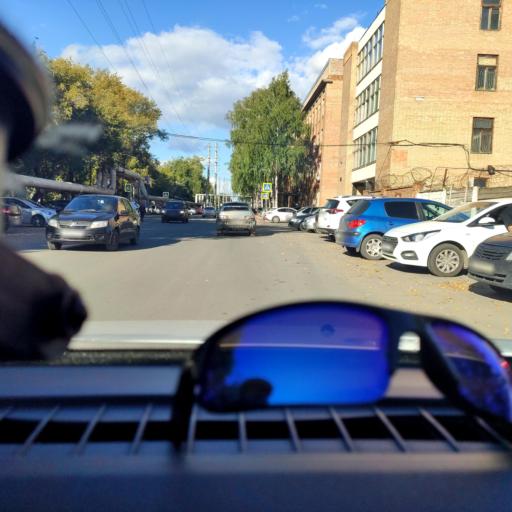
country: RU
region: Samara
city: Chapayevsk
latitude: 52.9758
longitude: 49.7157
